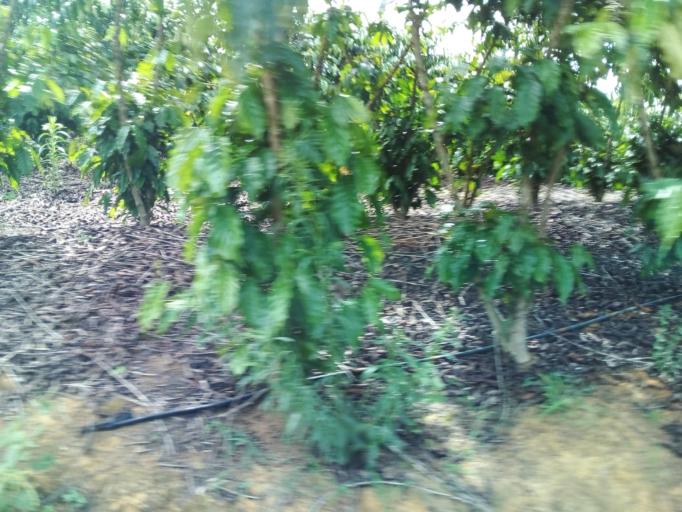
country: BR
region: Espirito Santo
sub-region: Santa Leopoldina
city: Santa Leopoldina
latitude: -20.0660
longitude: -40.4180
